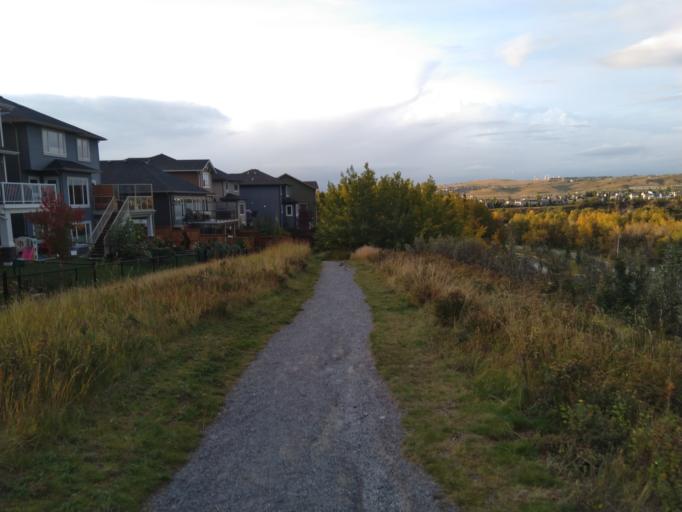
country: CA
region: Alberta
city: Cochrane
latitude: 51.1829
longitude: -114.5020
